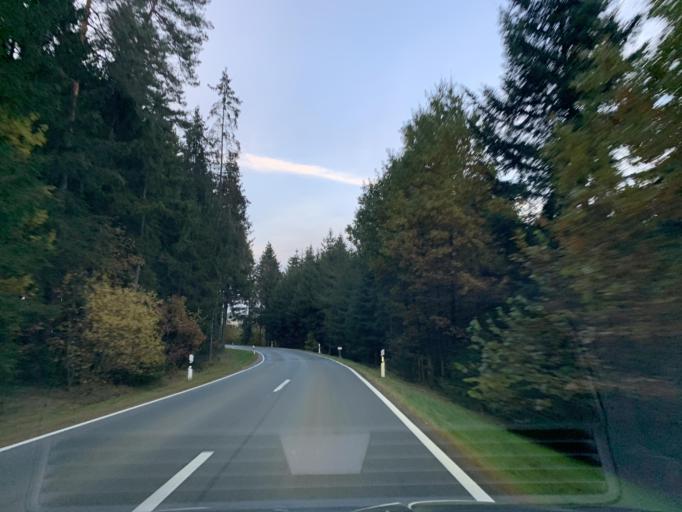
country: DE
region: Bavaria
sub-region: Upper Palatinate
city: Bach
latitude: 49.3902
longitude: 12.3962
